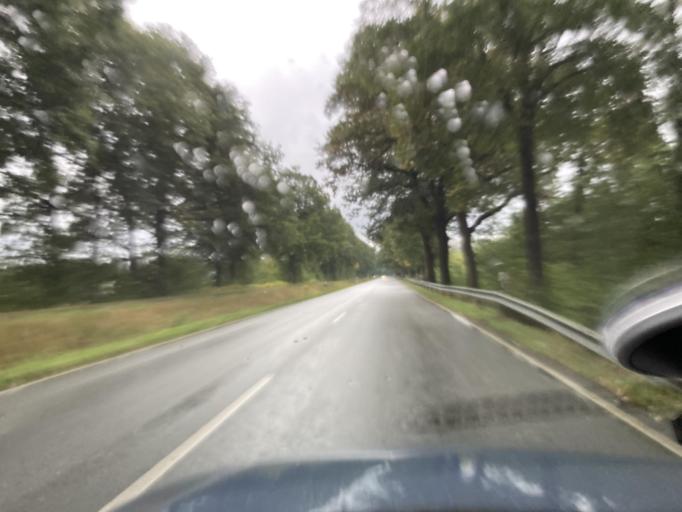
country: DE
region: Schleswig-Holstein
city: Nordhastedt
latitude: 54.1948
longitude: 9.1864
